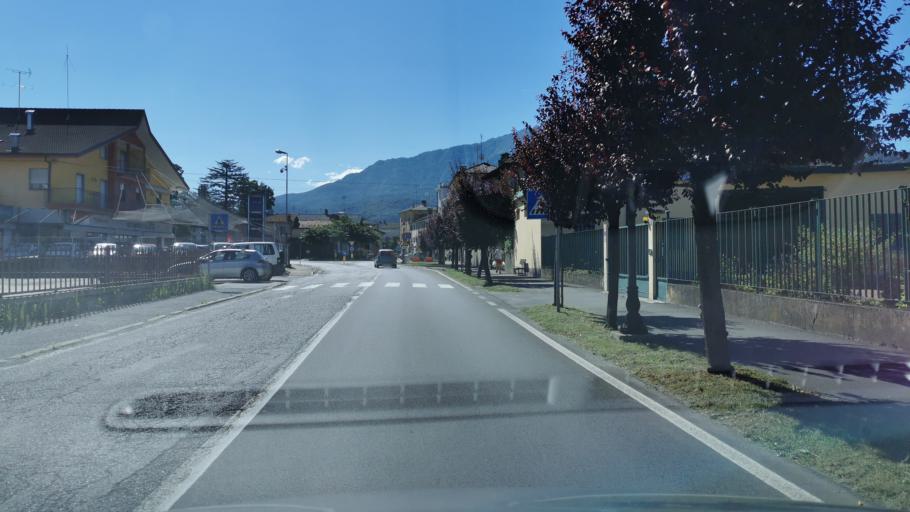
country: IT
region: Piedmont
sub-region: Provincia di Cuneo
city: Boves
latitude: 44.3321
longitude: 7.5476
